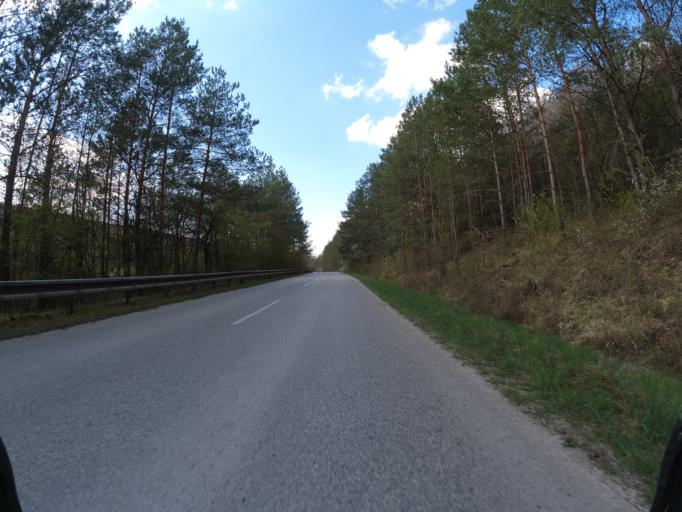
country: SK
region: Nitriansky
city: Stara Tura
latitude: 48.7555
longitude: 17.7173
